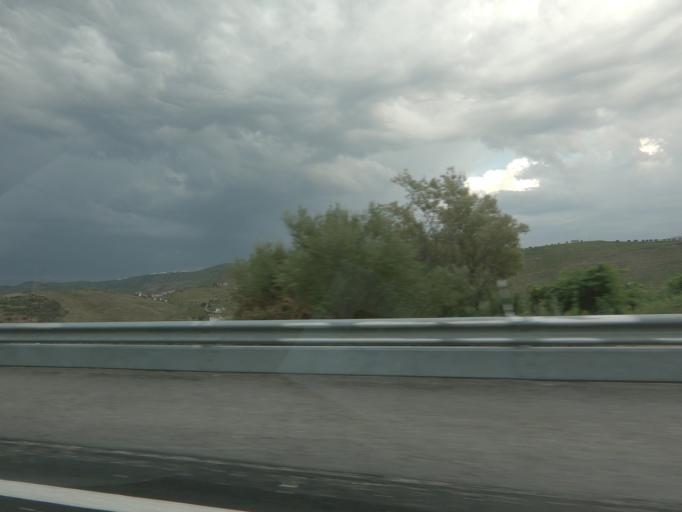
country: PT
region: Vila Real
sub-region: Peso da Regua
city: Peso da Regua
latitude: 41.1632
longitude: -7.7713
